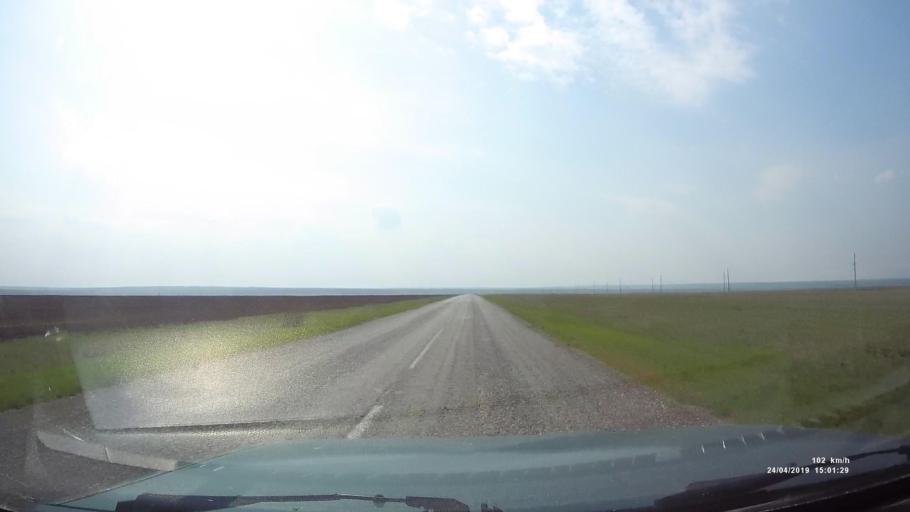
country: RU
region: Rostov
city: Remontnoye
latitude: 46.5661
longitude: 43.5328
